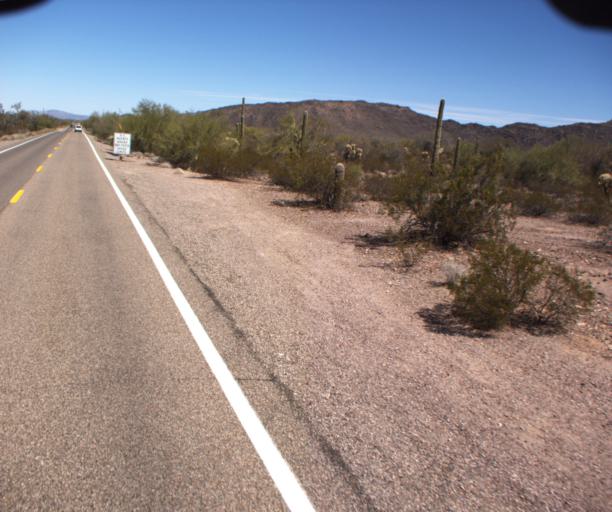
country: US
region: Arizona
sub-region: Pima County
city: Ajo
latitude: 32.1871
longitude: -112.7609
